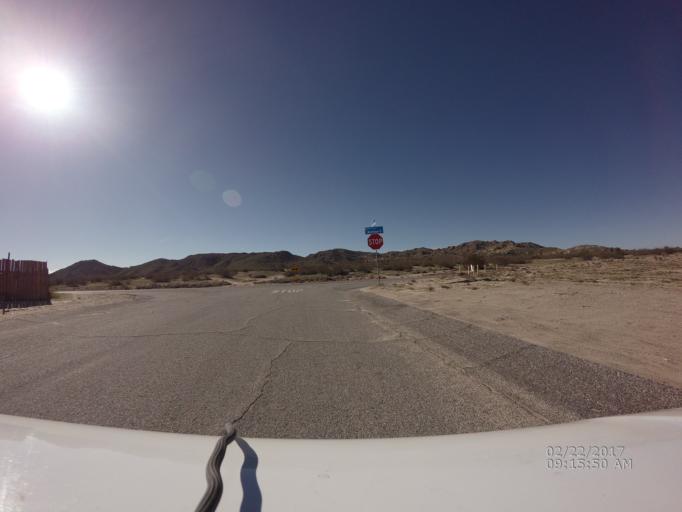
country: US
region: California
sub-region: Los Angeles County
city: Lake Los Angeles
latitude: 34.6168
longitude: -117.8491
